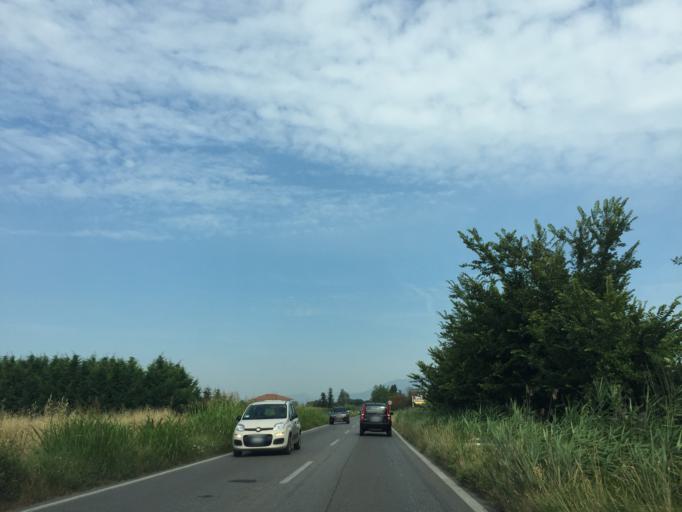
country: IT
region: Tuscany
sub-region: Provincia di Pistoia
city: Montecatini-Terme
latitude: 43.8549
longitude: 10.7790
